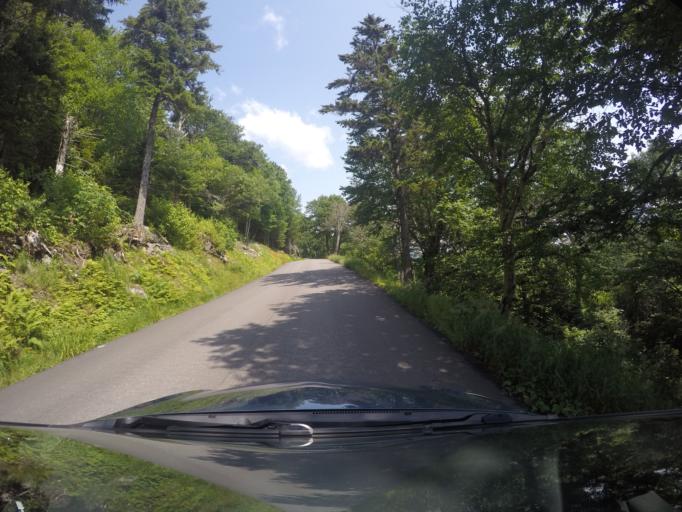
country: US
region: New Hampshire
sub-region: Coos County
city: Gorham
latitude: 44.2818
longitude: -71.2566
